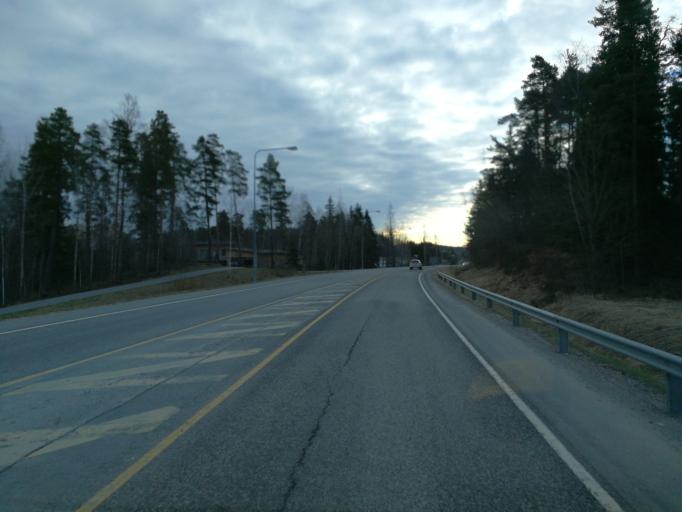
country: FI
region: Varsinais-Suomi
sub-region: Turku
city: Piikkioe
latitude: 60.4207
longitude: 22.4604
